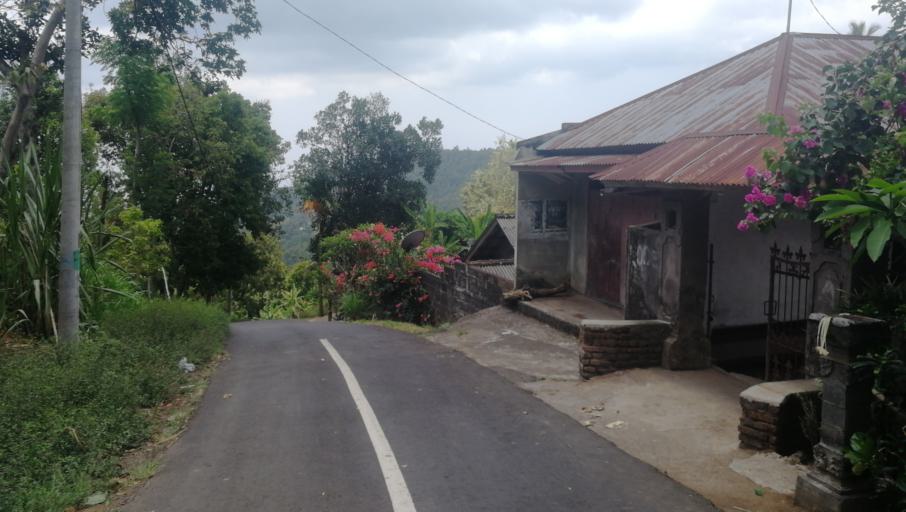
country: ID
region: Bali
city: Munduk
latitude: -8.2955
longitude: 115.0475
